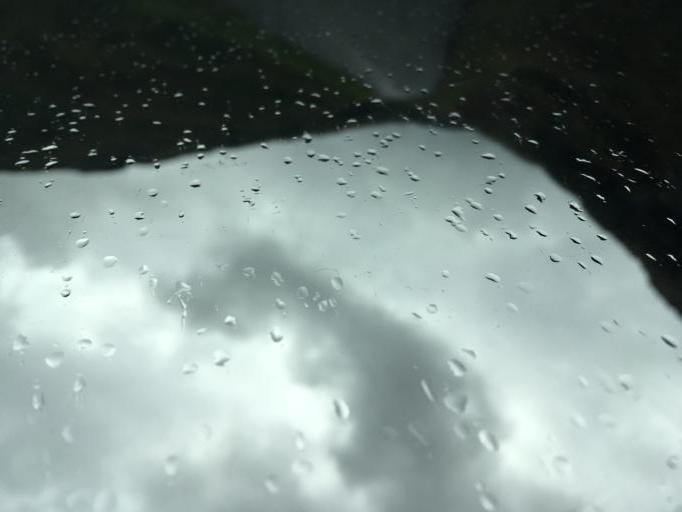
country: GB
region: Scotland
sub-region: Argyll and Bute
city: Oban
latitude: 56.2577
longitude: -5.4617
